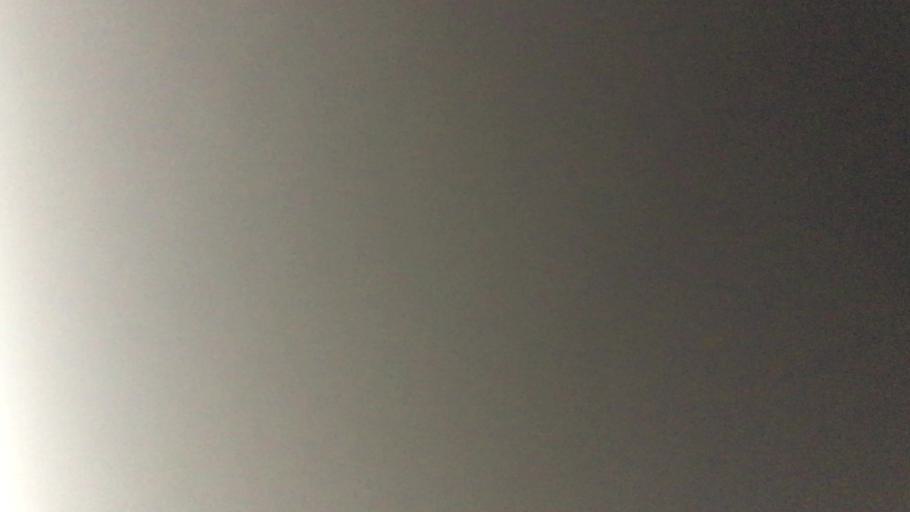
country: US
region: New York
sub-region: Erie County
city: Alden
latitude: 42.9577
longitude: -78.4058
